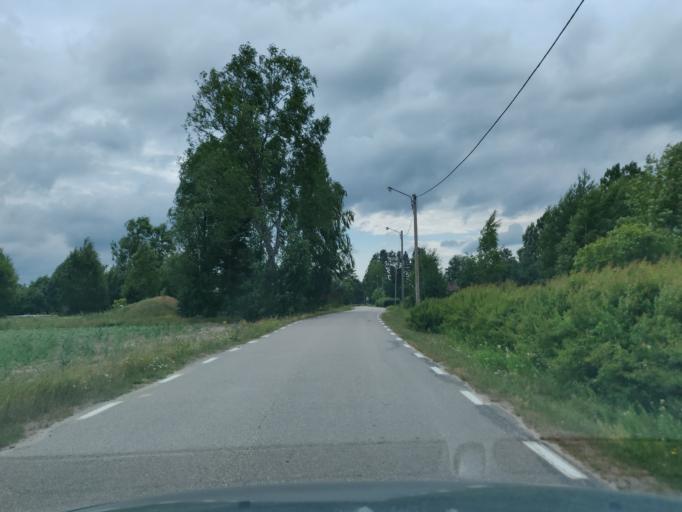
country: SE
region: Vaermland
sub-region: Munkfors Kommun
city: Munkfors
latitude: 59.8826
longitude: 13.5603
